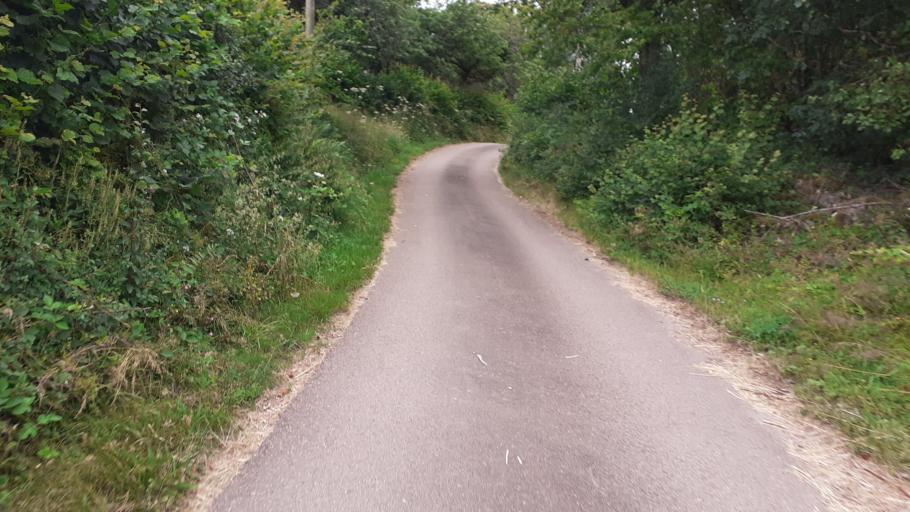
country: FR
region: Bourgogne
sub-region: Departement de la Cote-d'Or
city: Saulieu
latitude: 47.2697
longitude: 4.1407
